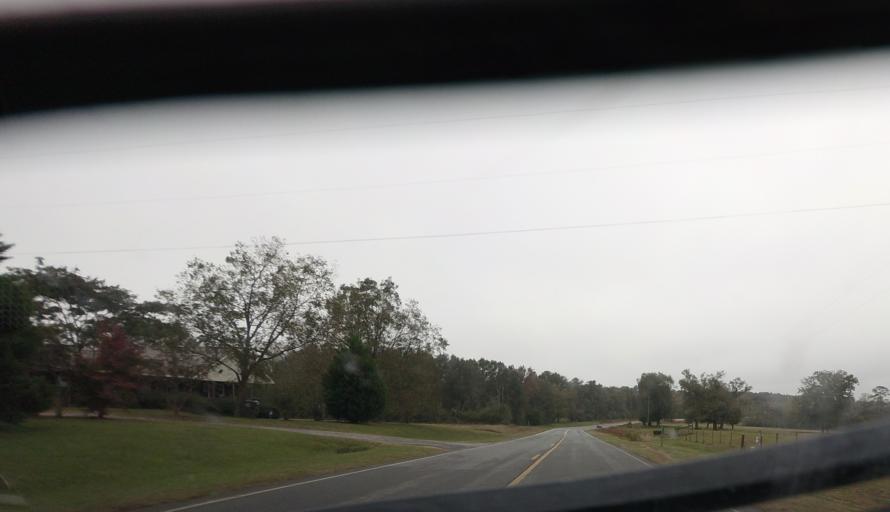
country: US
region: Georgia
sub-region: Marion County
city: Buena Vista
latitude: 32.3709
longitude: -84.4567
